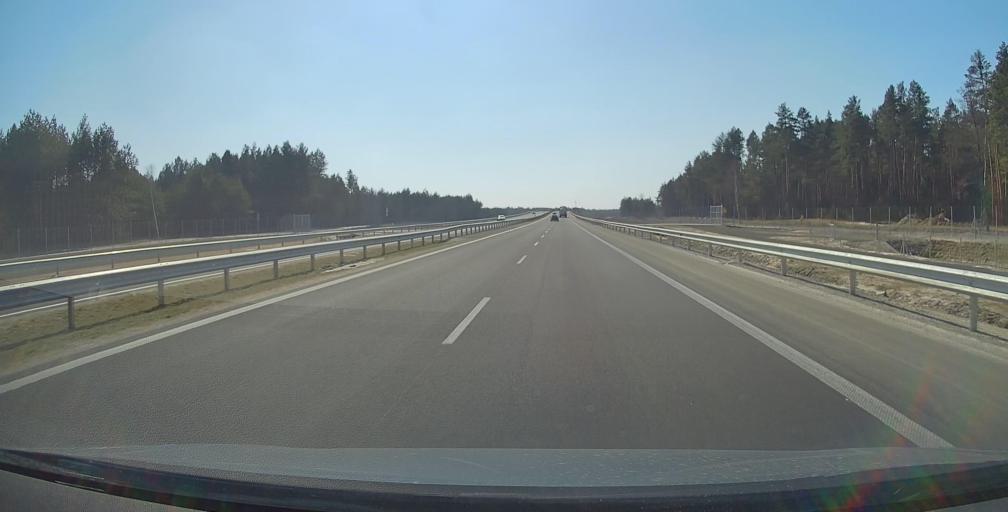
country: PL
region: Subcarpathian Voivodeship
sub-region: Powiat nizanski
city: Konczyce
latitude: 50.4448
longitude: 22.1403
